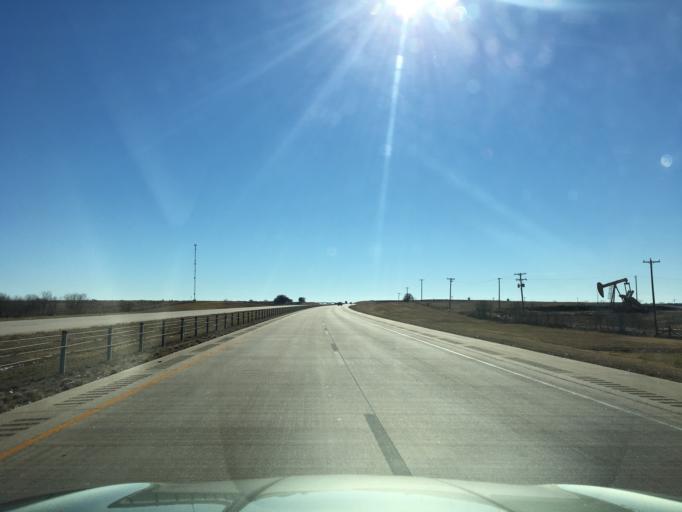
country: US
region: Oklahoma
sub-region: Kay County
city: Tonkawa
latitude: 36.5179
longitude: -97.3376
